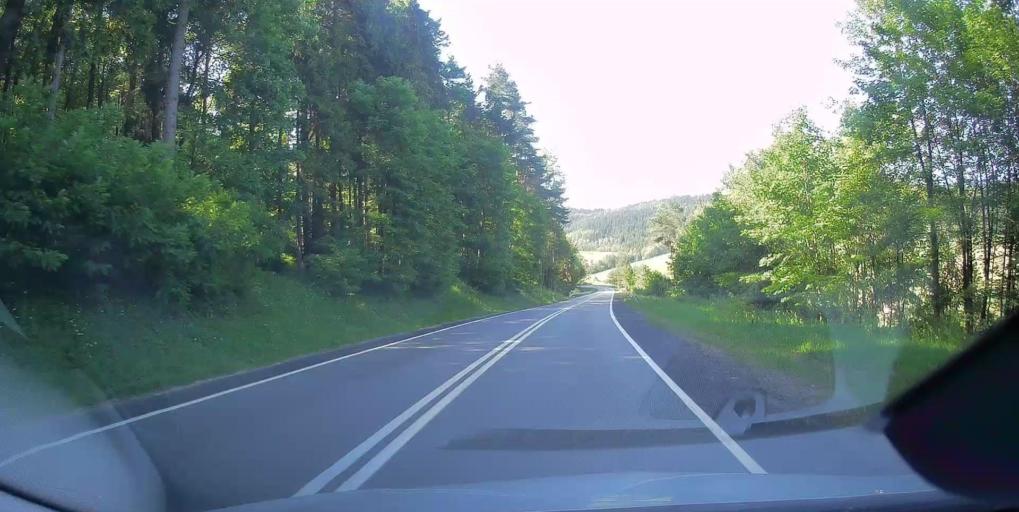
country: PL
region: Lesser Poland Voivodeship
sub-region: Powiat nowosadecki
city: Krynica-Zdroj
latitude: 49.4701
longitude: 20.9458
